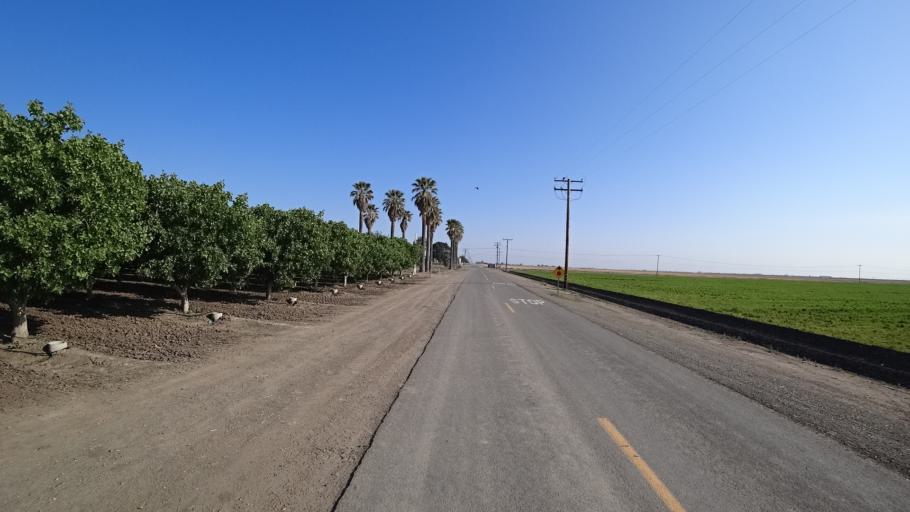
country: US
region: California
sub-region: Kings County
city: Home Garden
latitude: 36.2682
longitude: -119.5294
